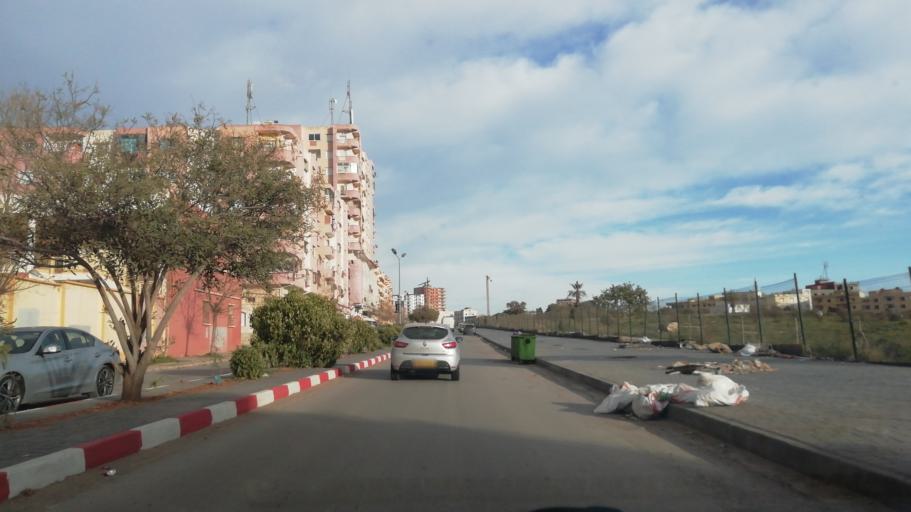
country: DZ
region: Oran
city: Bir el Djir
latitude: 35.7207
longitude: -0.5898
